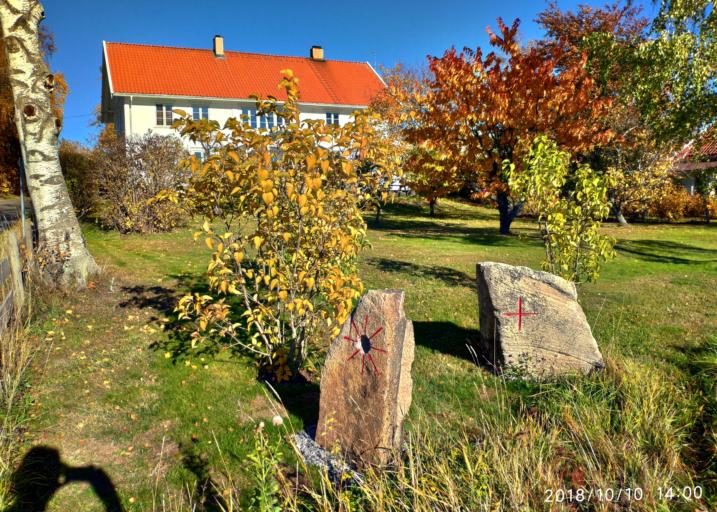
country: NO
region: Akershus
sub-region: Nannestad
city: Teigebyen
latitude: 60.1997
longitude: 11.0342
